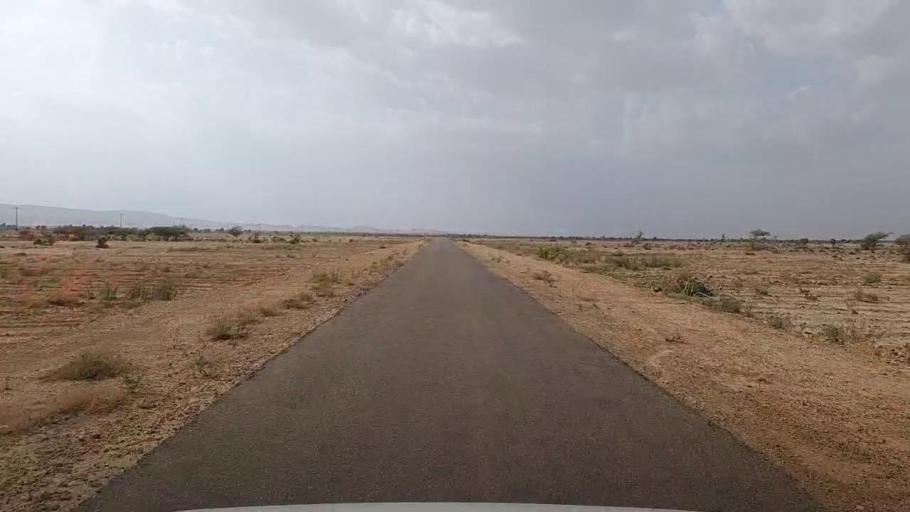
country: PK
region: Sindh
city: Jamshoro
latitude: 25.4420
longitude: 67.6827
